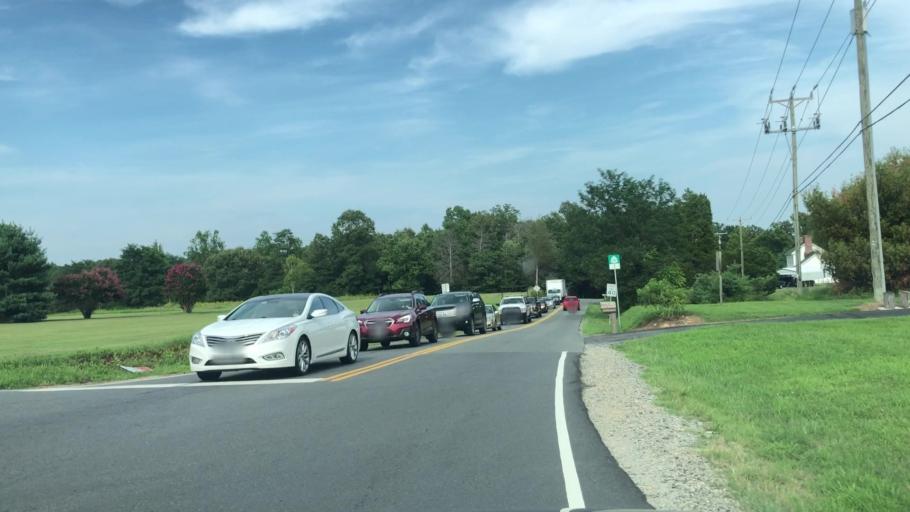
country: US
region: Virginia
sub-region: Stafford County
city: Stafford
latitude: 38.4224
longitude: -77.4771
